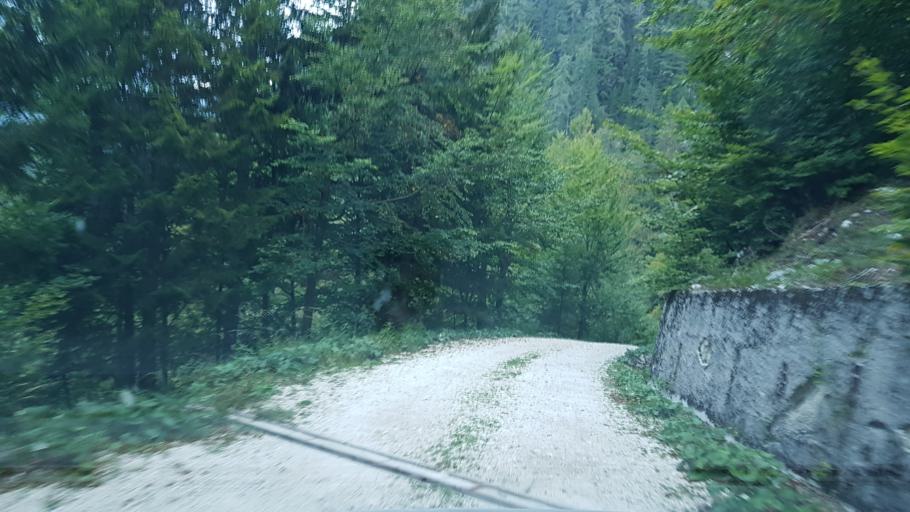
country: SI
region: Bovec
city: Bovec
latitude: 46.4034
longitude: 13.5091
